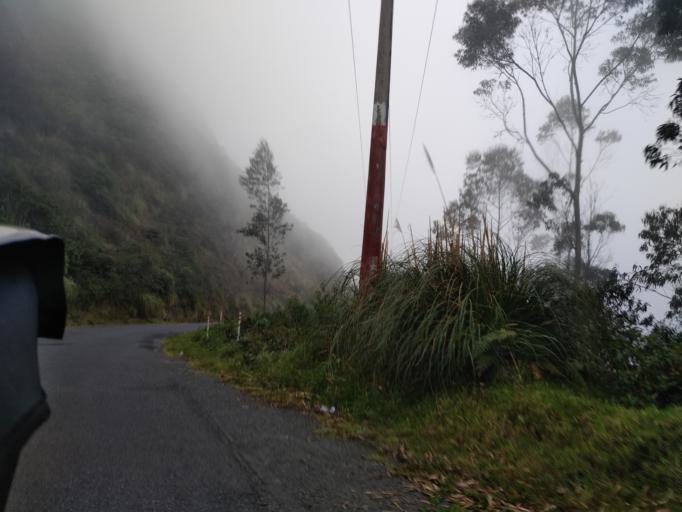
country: EC
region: Cotopaxi
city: Saquisili
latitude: -0.6882
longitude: -78.8292
